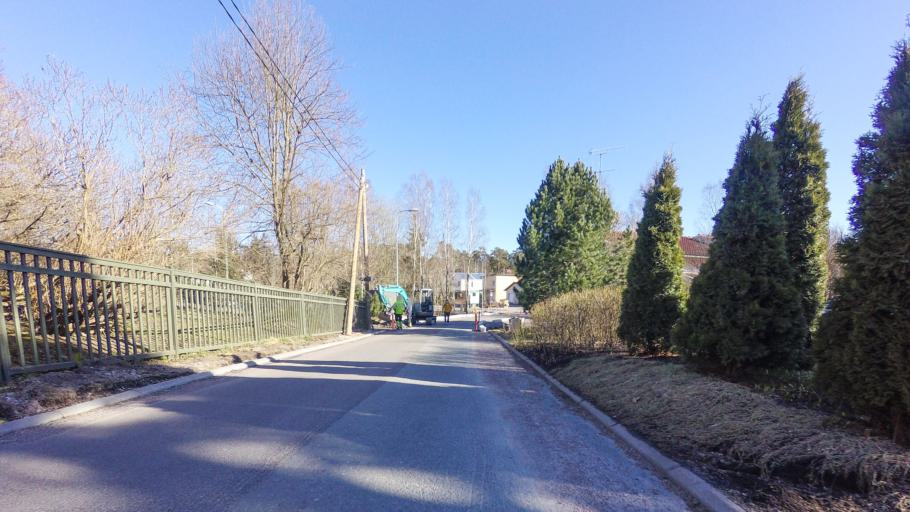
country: FI
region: Uusimaa
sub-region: Helsinki
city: Helsinki
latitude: 60.1739
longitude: 25.0204
